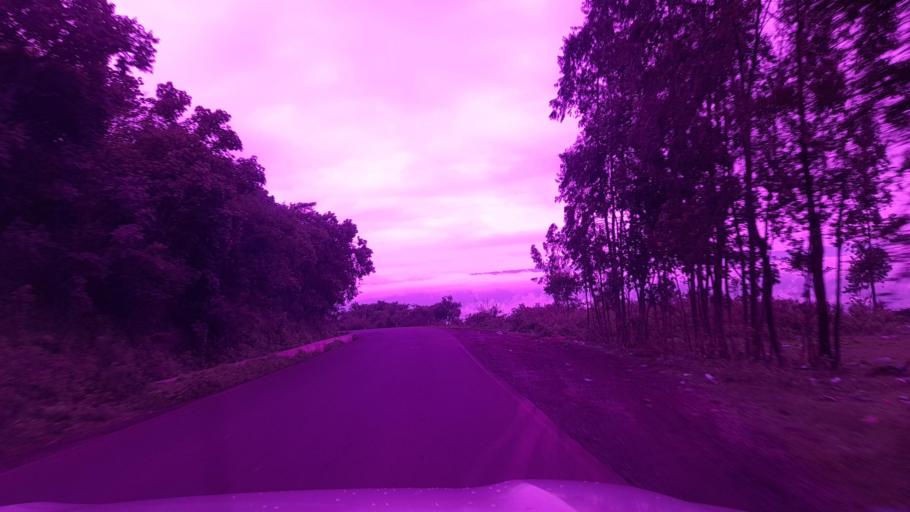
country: ET
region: Oromiya
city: Waliso
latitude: 8.1718
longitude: 37.5821
